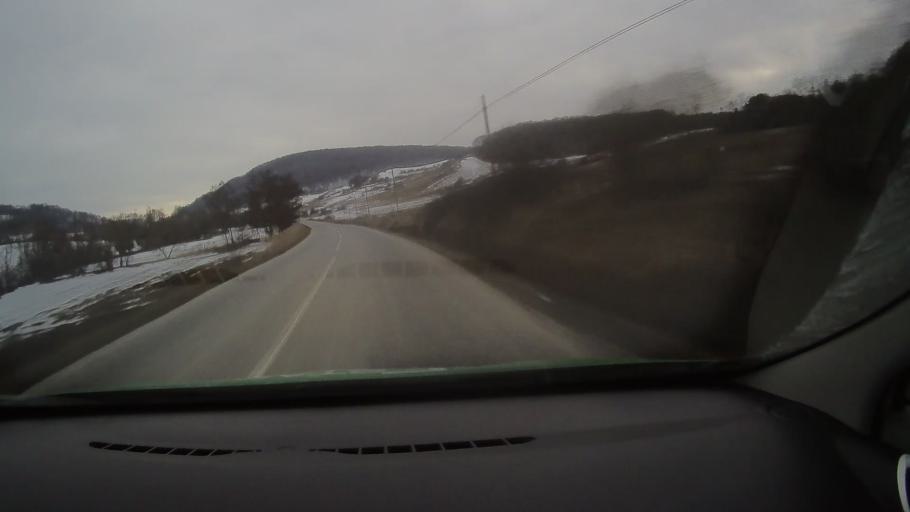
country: RO
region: Harghita
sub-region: Comuna Mugeni
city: Mugeni
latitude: 46.2318
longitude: 25.2414
